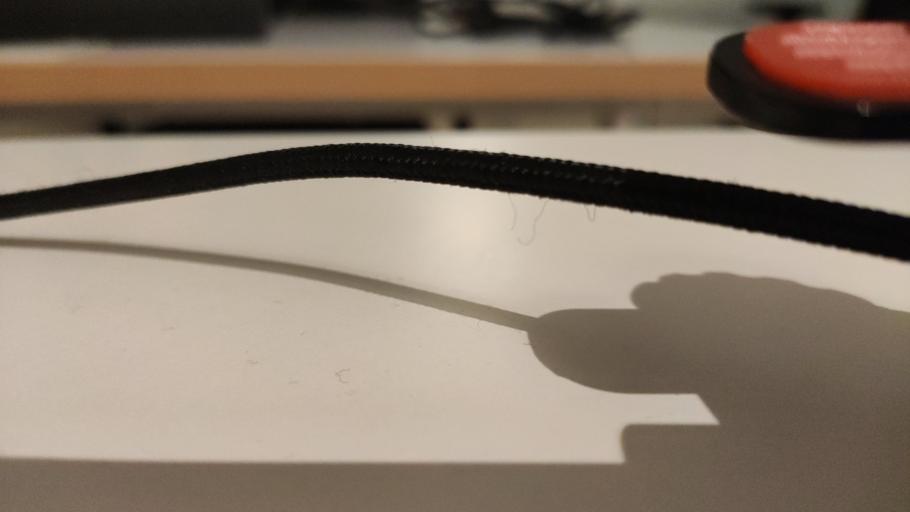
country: RU
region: Moskovskaya
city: Dmitrov
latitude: 56.3628
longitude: 37.5340
